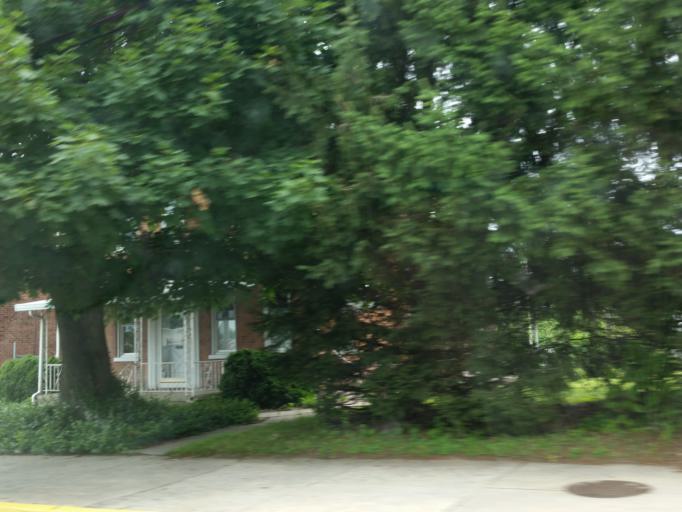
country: US
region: Pennsylvania
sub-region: York County
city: North York
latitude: 39.9751
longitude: -76.7323
